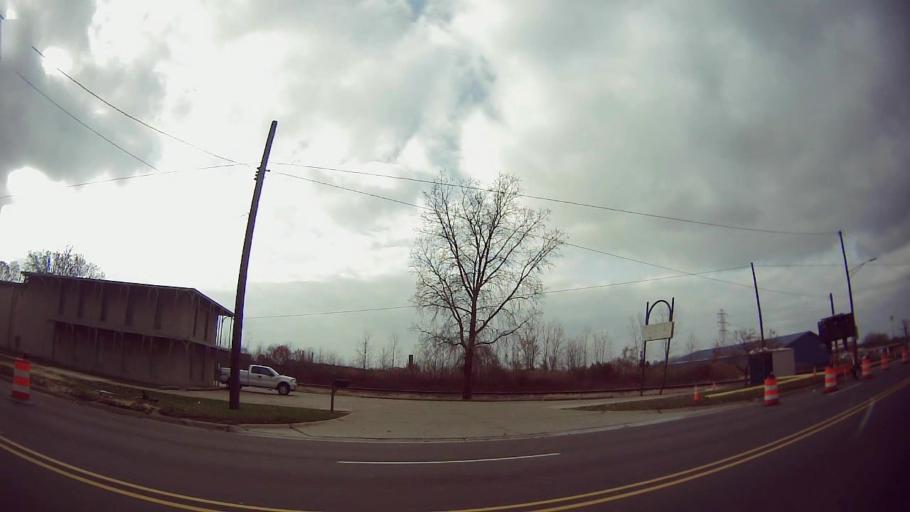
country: US
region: Michigan
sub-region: Macomb County
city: Eastpointe
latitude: 42.4736
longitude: -82.9865
